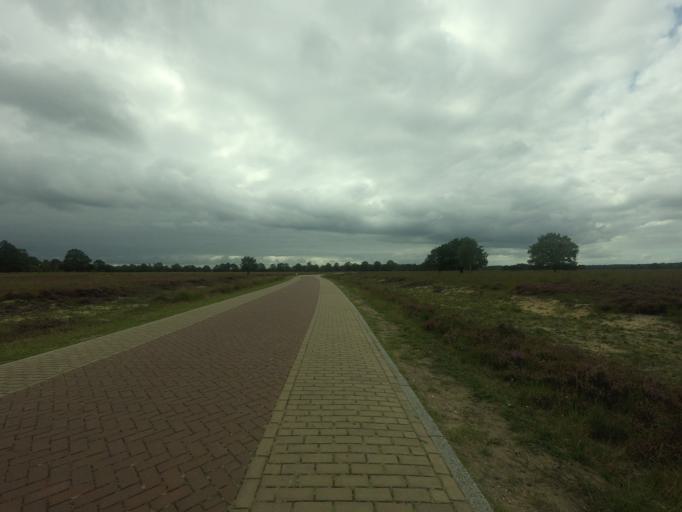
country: NL
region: Drenthe
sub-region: Gemeente Westerveld
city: Dwingeloo
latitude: 52.8994
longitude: 6.2676
